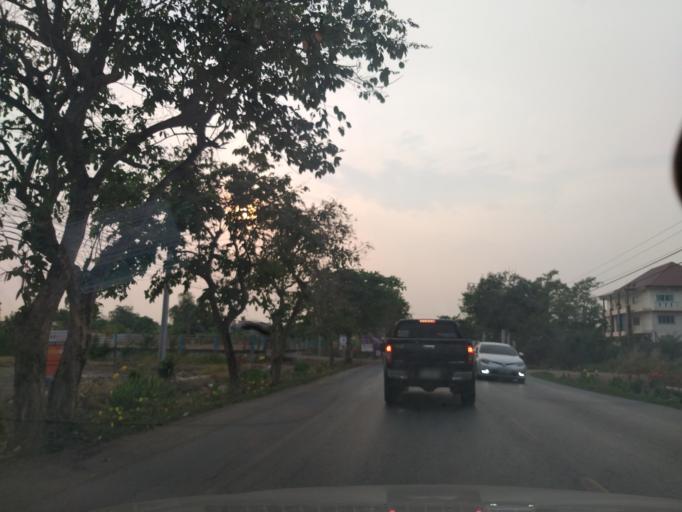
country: TH
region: Bangkok
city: Nong Chok
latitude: 13.8496
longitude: 100.8863
